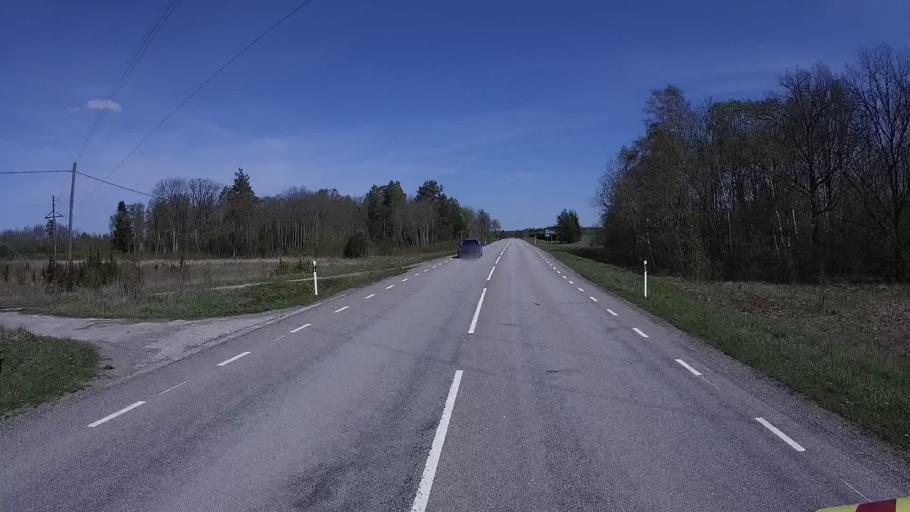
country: EE
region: Laeaene
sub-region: Ridala Parish
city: Uuemoisa
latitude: 58.9807
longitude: 23.6837
